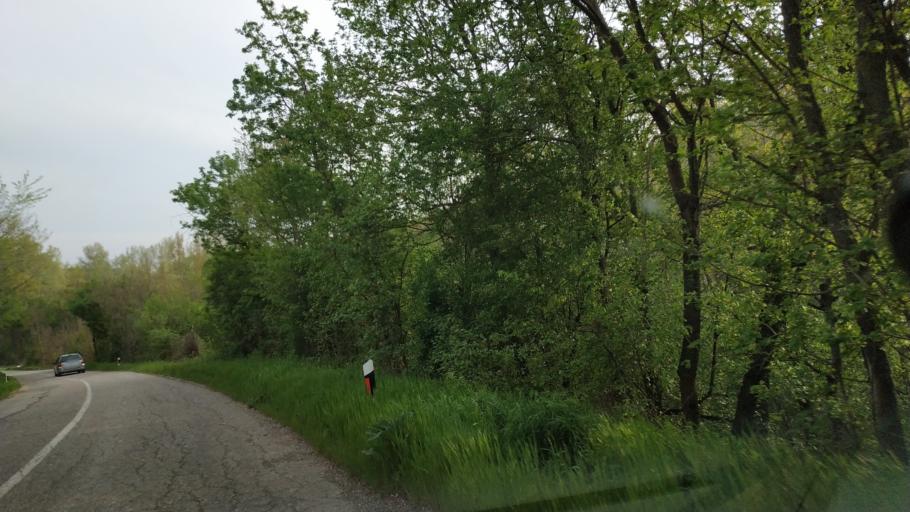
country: RS
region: Central Serbia
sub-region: Nisavski Okrug
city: Aleksinac
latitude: 43.4759
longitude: 21.8105
